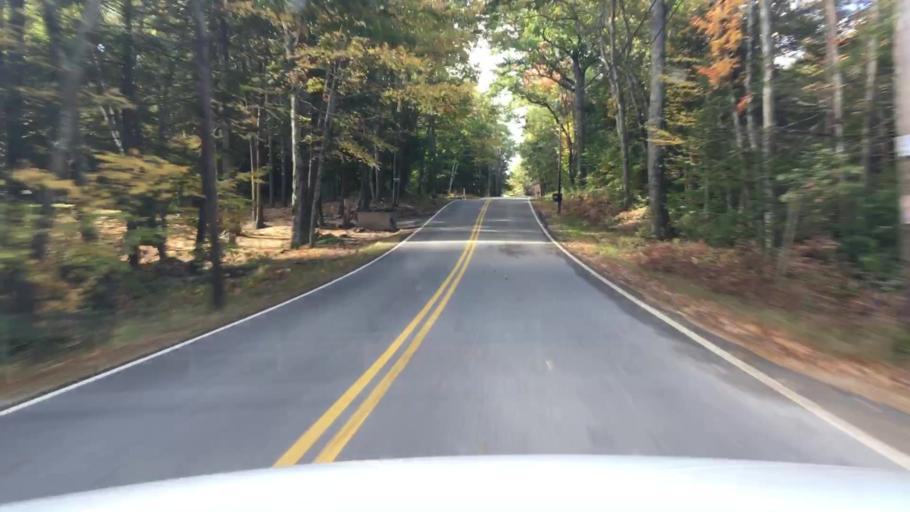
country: US
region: New Hampshire
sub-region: Strafford County
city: Barrington
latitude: 43.1703
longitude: -71.0495
